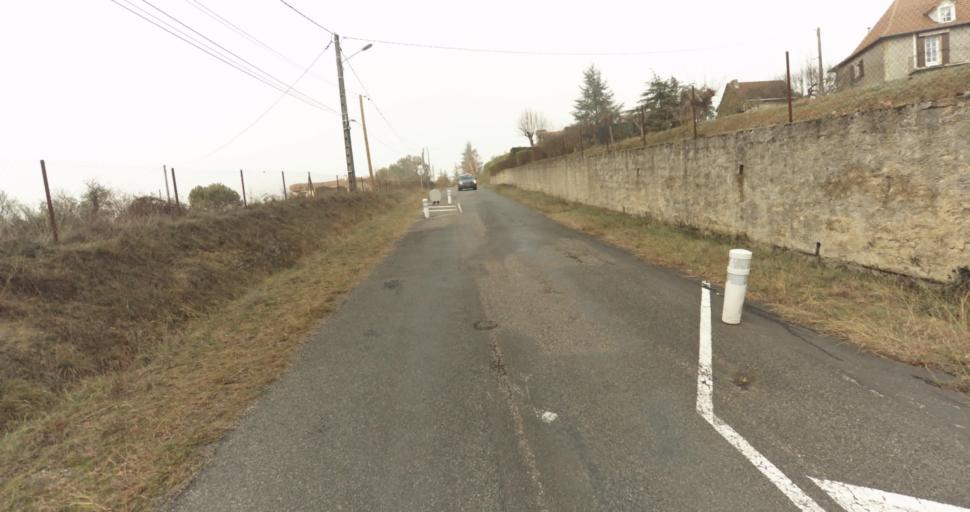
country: FR
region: Midi-Pyrenees
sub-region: Departement du Lot
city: Figeac
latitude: 44.6185
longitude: 2.0249
